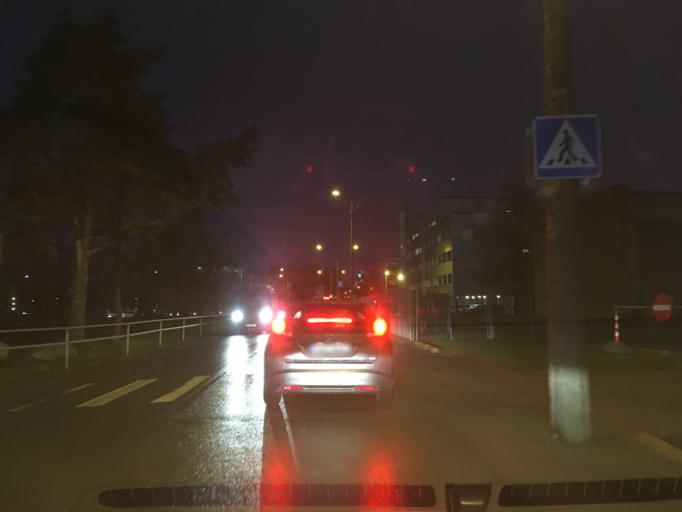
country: EE
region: Harju
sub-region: Saue vald
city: Laagri
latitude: 59.3962
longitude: 24.6630
